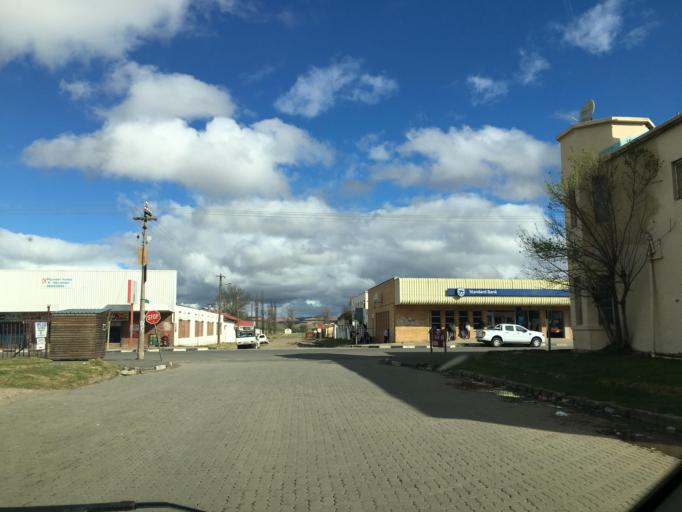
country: ZA
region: Eastern Cape
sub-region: Chris Hani District Municipality
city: Elliot
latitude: -31.3330
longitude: 27.8518
